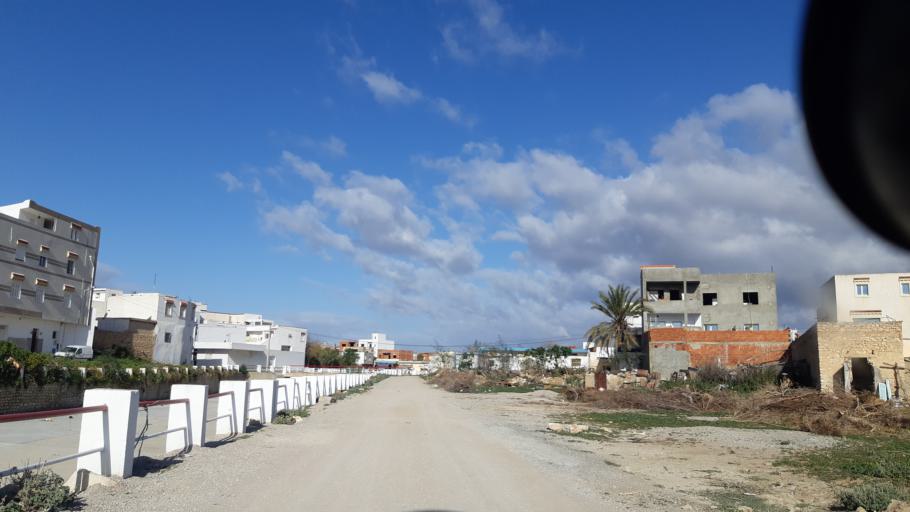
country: TN
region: Susah
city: Akouda
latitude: 35.8714
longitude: 10.5468
